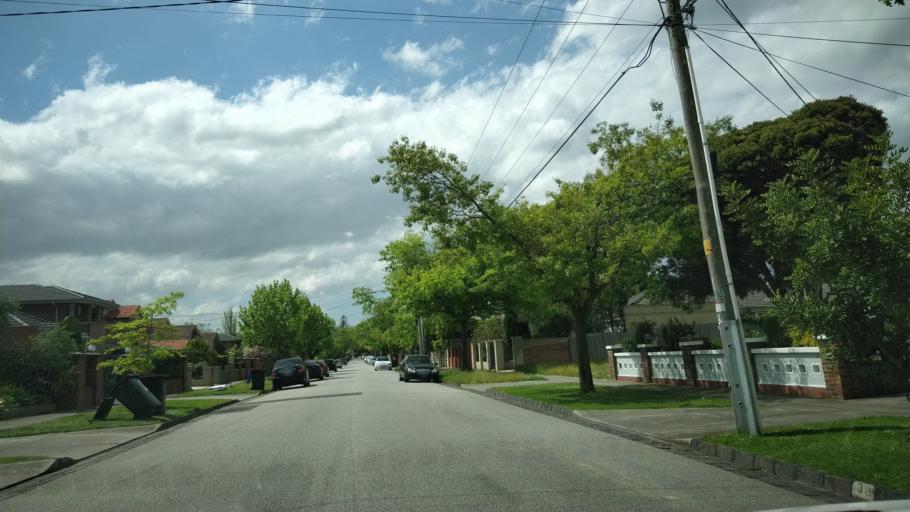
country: AU
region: Victoria
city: Glen Huntly
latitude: -37.8799
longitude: 145.0550
